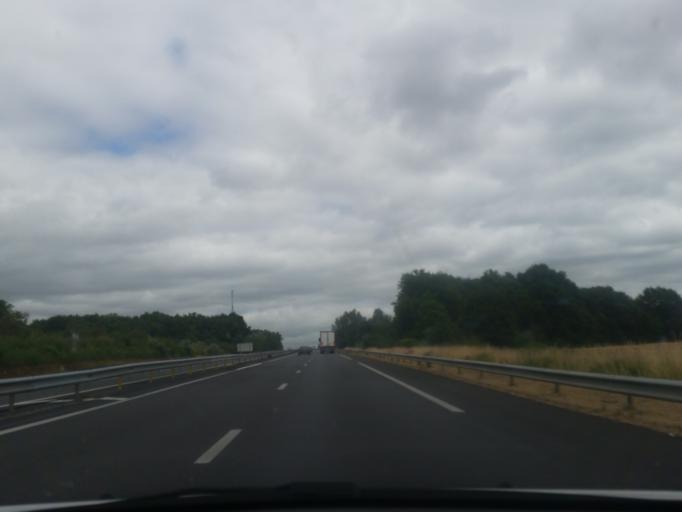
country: FR
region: Pays de la Loire
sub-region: Departement de Maine-et-Loire
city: Seiches-sur-le-Loir
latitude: 47.6000
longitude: -0.3095
